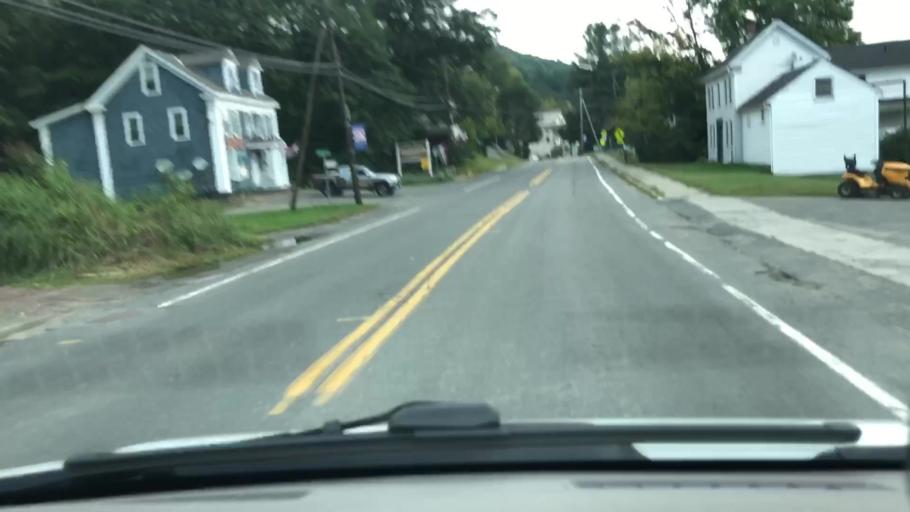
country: US
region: Massachusetts
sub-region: Franklin County
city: Charlemont
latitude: 42.6276
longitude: -72.8769
